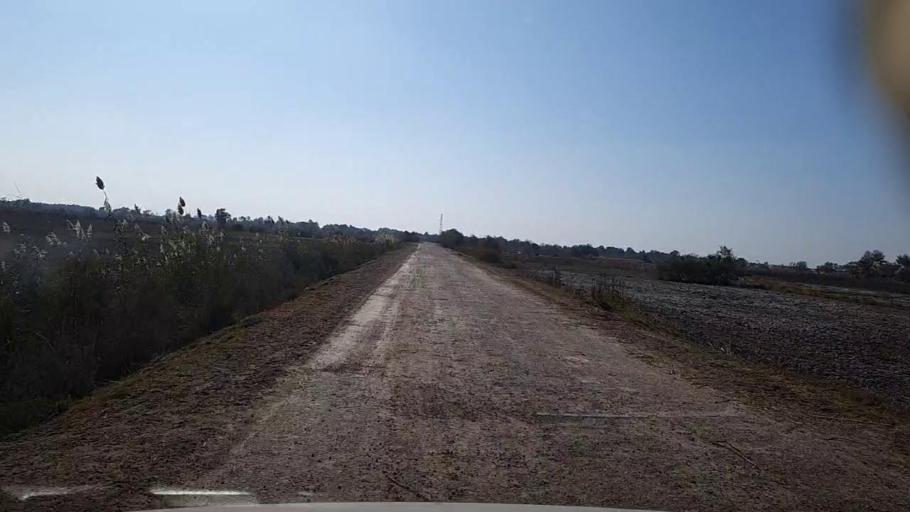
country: PK
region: Sindh
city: Khairpur
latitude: 27.9448
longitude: 69.7286
